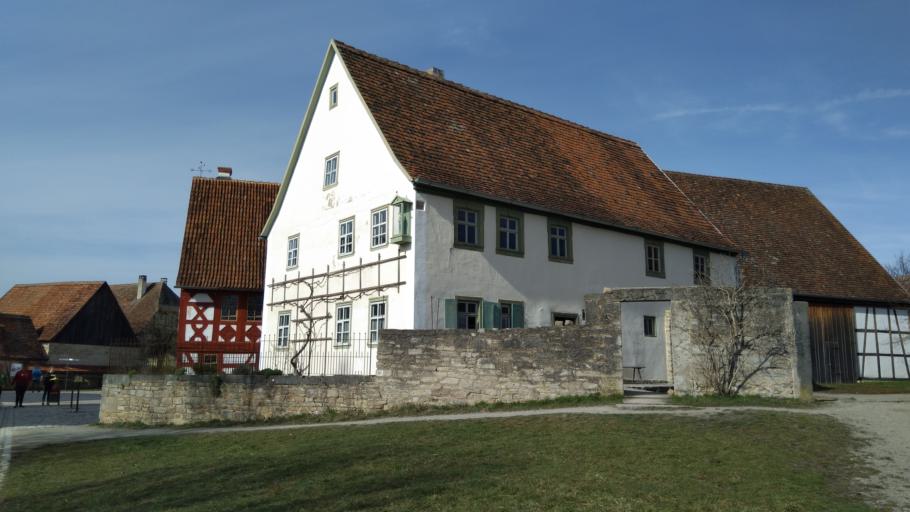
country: DE
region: Bavaria
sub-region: Regierungsbezirk Mittelfranken
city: Bad Windsheim
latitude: 49.4952
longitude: 10.4182
